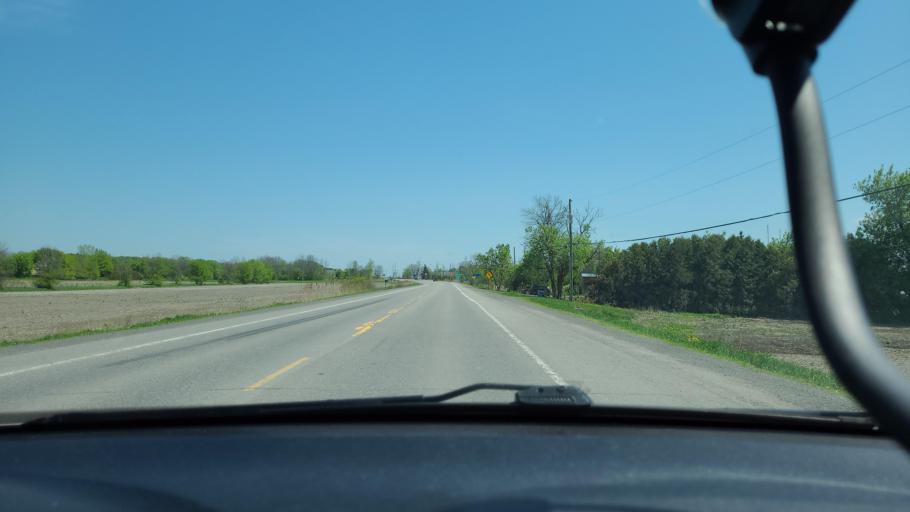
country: CA
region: Quebec
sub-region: Laurentides
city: Mirabel
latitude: 45.6224
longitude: -74.1084
